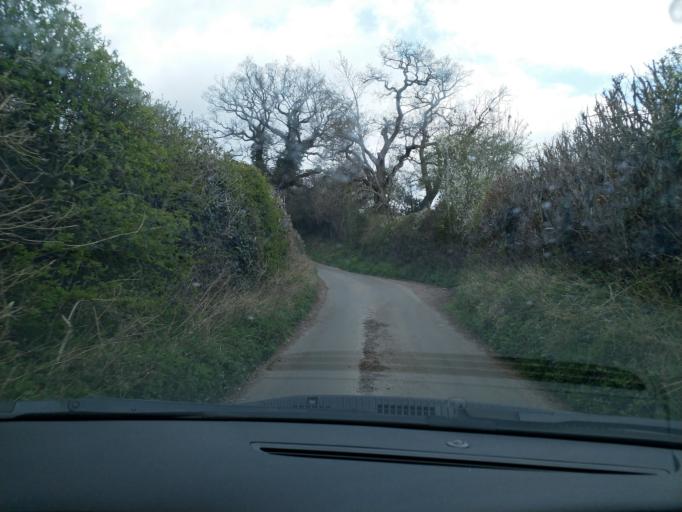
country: GB
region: England
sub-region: Warwickshire
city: Henley in Arden
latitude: 52.2907
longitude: -1.7454
